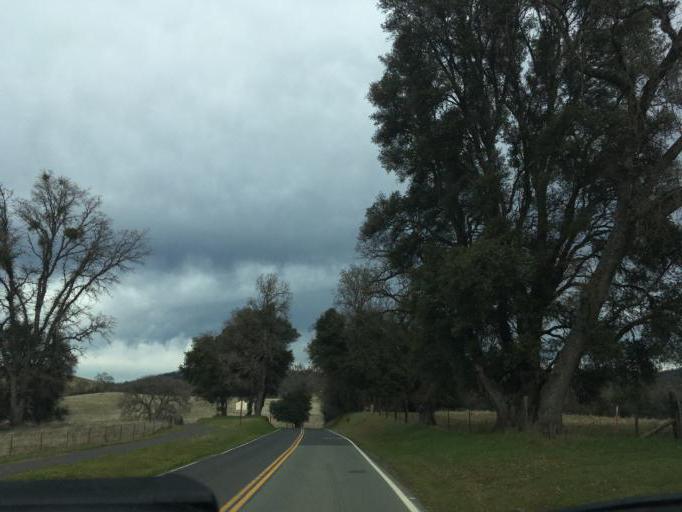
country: US
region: California
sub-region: Calaveras County
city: Mountain Ranch
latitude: 38.2229
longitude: -120.5467
